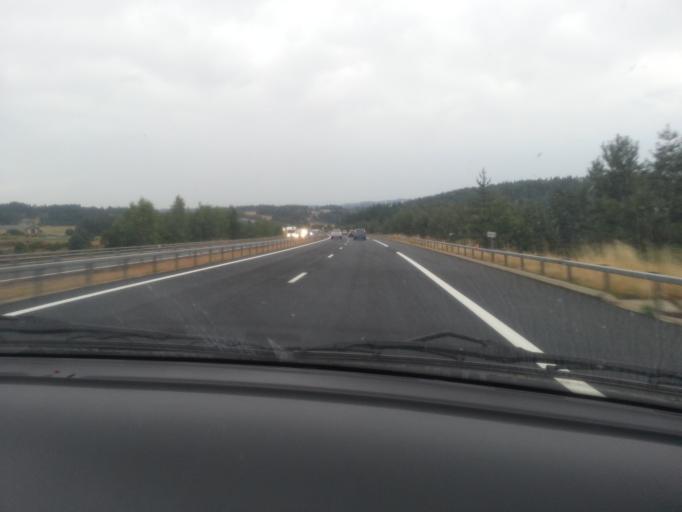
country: FR
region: Languedoc-Roussillon
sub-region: Departement de la Lozere
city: Aumont-Aubrac
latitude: 44.6607
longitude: 3.2579
